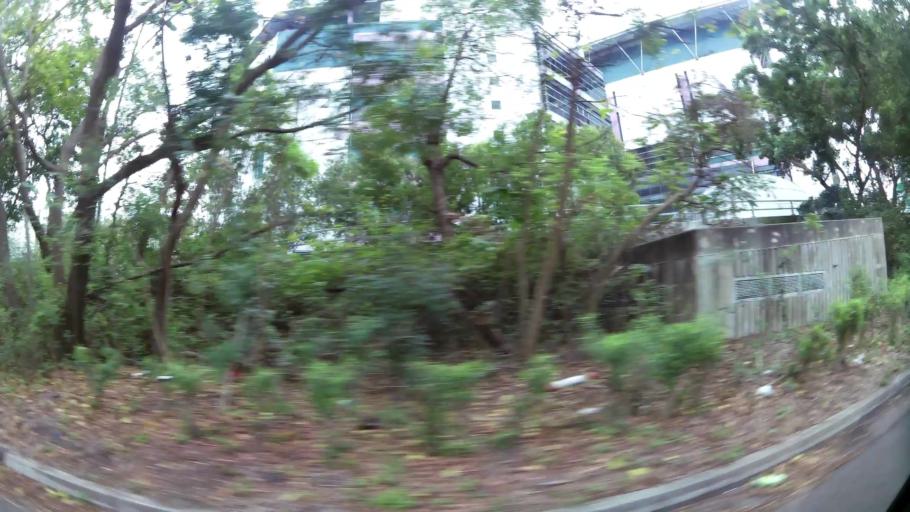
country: HK
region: Wanchai
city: Wan Chai
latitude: 22.2850
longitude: 114.2216
